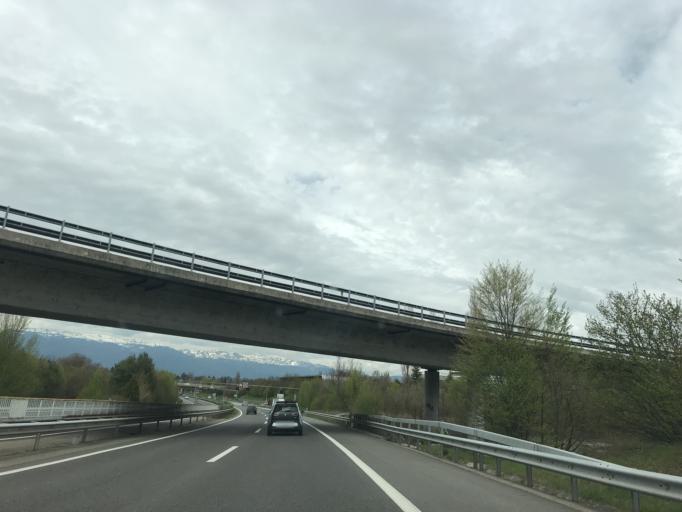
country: CH
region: Geneva
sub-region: Geneva
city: Plan-les-Ouates
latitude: 46.1627
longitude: 6.1010
